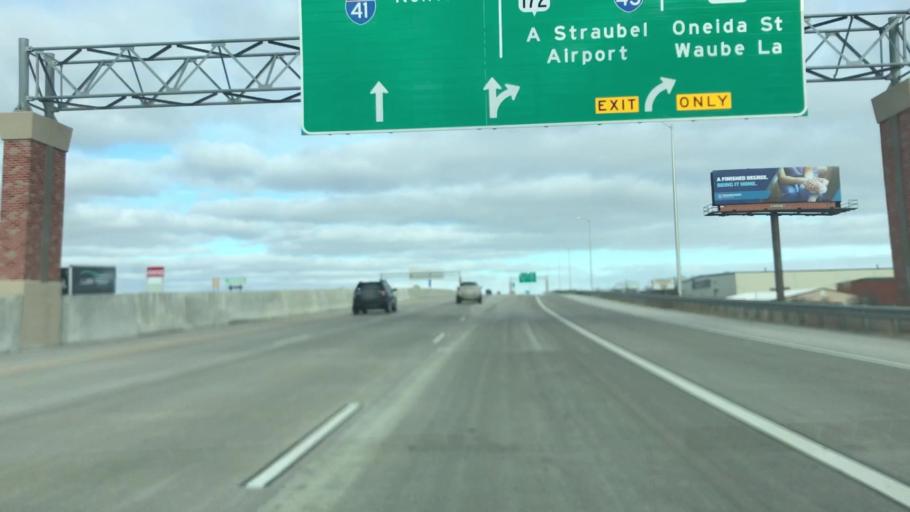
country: US
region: Wisconsin
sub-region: Brown County
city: Ashwaubenon
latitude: 44.4622
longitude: -88.0831
